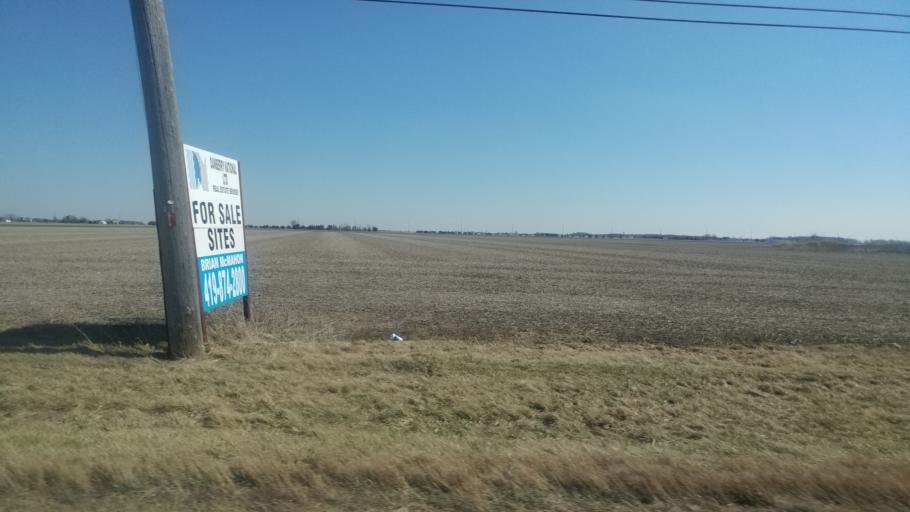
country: US
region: Ohio
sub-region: Wood County
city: Perrysburg
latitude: 41.5008
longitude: -83.6421
